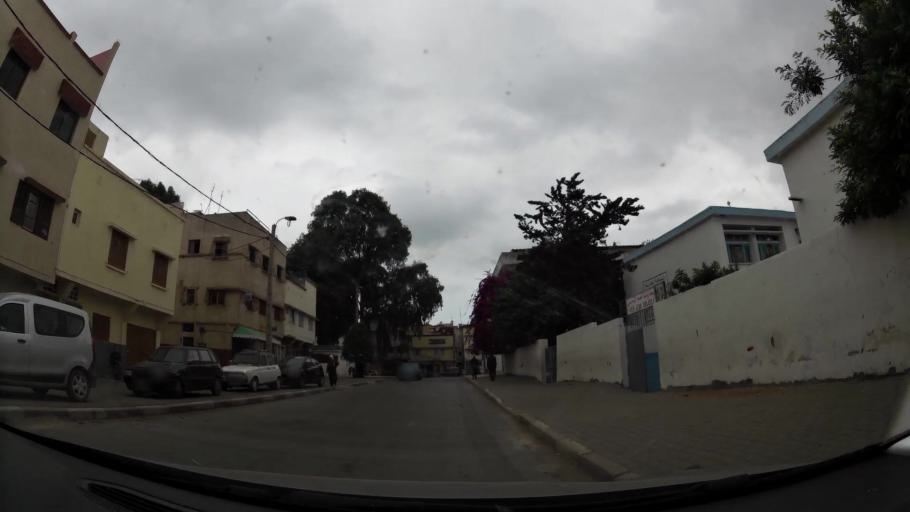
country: MA
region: Rabat-Sale-Zemmour-Zaer
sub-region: Rabat
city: Rabat
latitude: 33.9823
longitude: -6.8235
